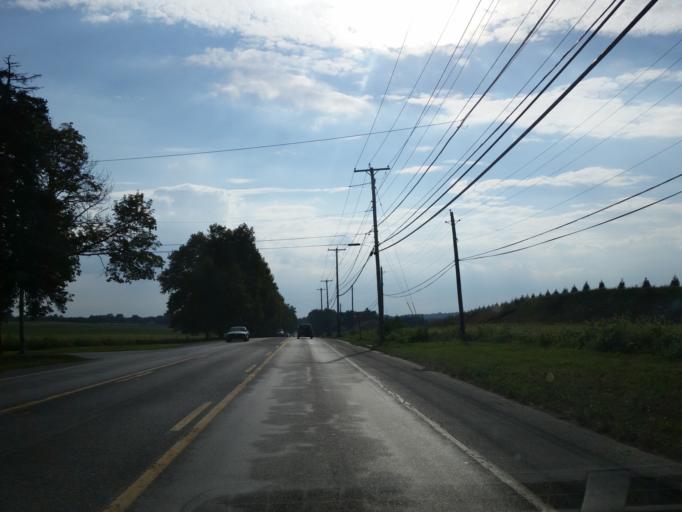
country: US
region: Pennsylvania
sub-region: Lebanon County
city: Annville
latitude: 40.3238
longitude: -76.5426
